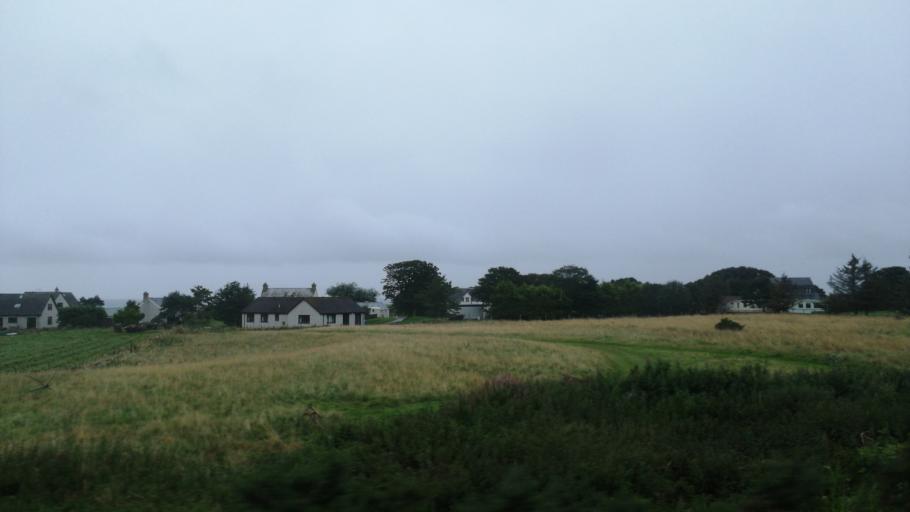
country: GB
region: Scotland
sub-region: Highland
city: Brora
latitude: 58.0296
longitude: -3.8476
